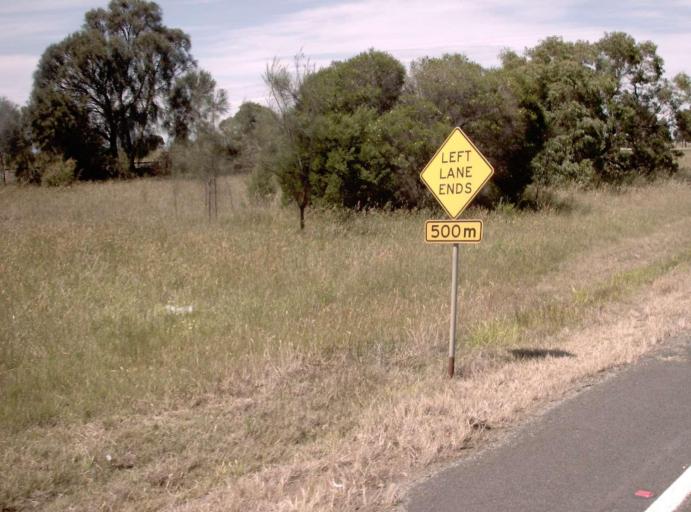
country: AU
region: Victoria
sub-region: Wellington
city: Sale
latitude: -38.1023
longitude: 146.9414
